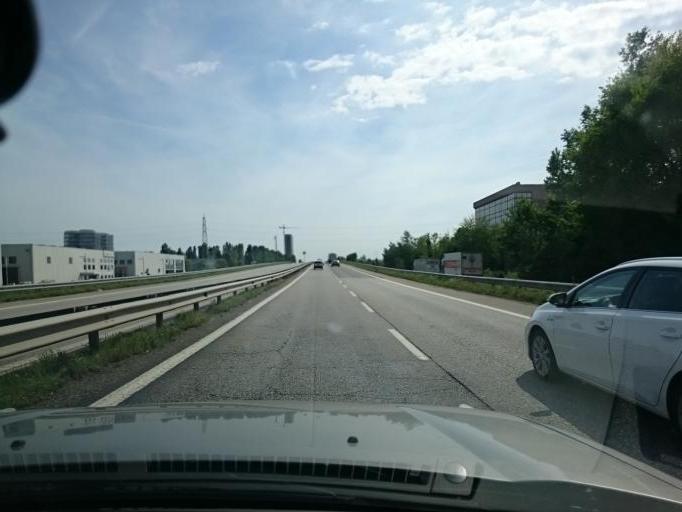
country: IT
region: Veneto
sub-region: Provincia di Padova
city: Noventa
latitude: 45.3981
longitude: 11.9296
